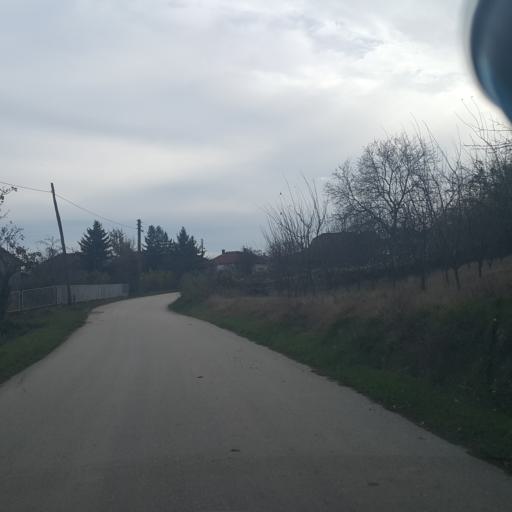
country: RS
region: Central Serbia
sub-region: Zajecarski Okrug
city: Knjazevac
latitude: 43.6012
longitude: 22.2578
